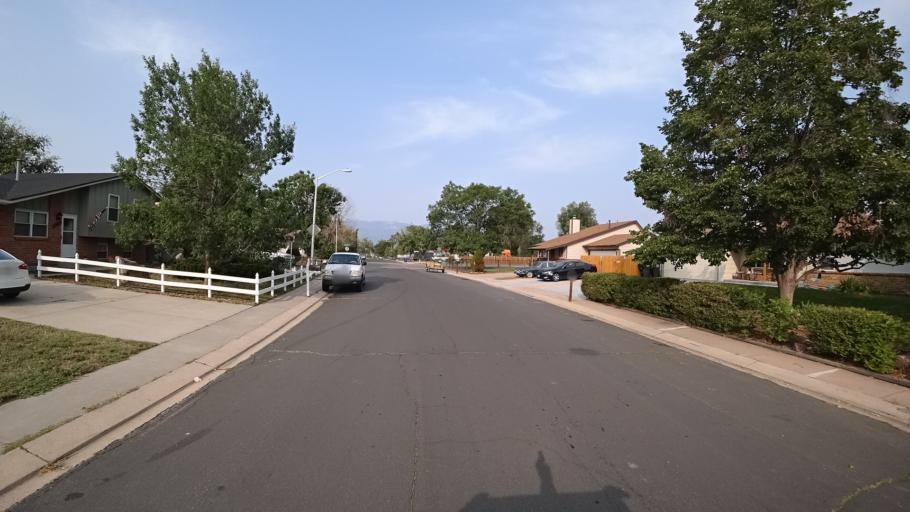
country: US
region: Colorado
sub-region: El Paso County
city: Stratmoor
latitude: 38.7995
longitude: -104.7424
